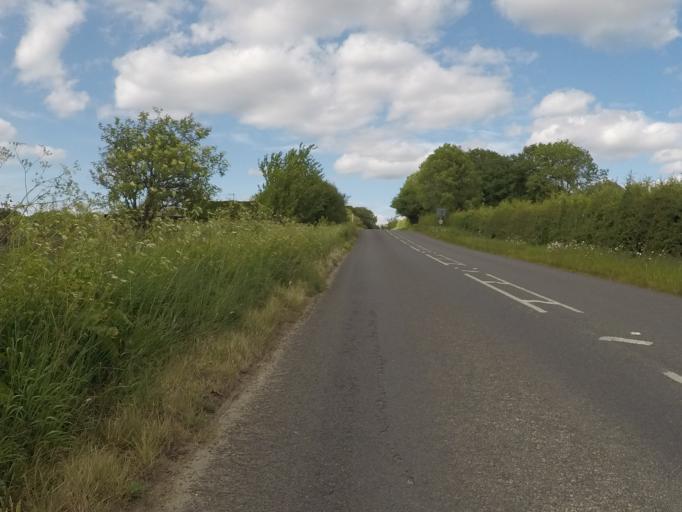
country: GB
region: England
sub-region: Oxfordshire
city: Charlbury
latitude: 51.8385
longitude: -1.4960
